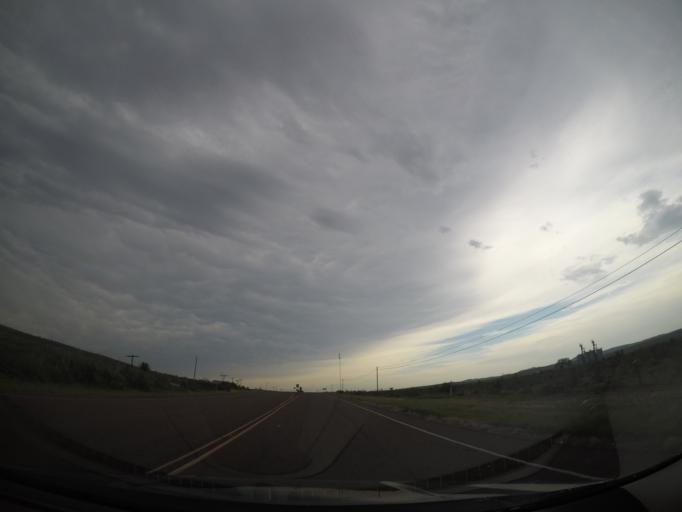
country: US
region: Texas
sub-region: Brewster County
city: Alpine
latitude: 30.2059
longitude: -103.2243
